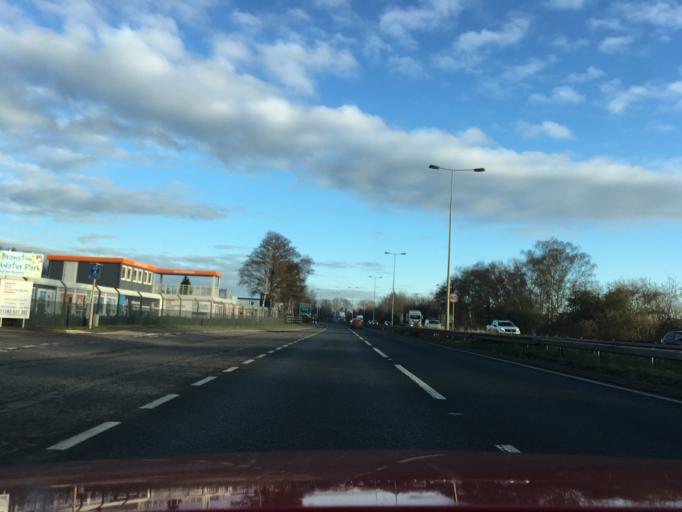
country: GB
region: England
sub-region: Staffordshire
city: Burton upon Trent
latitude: 52.7832
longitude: -1.6790
